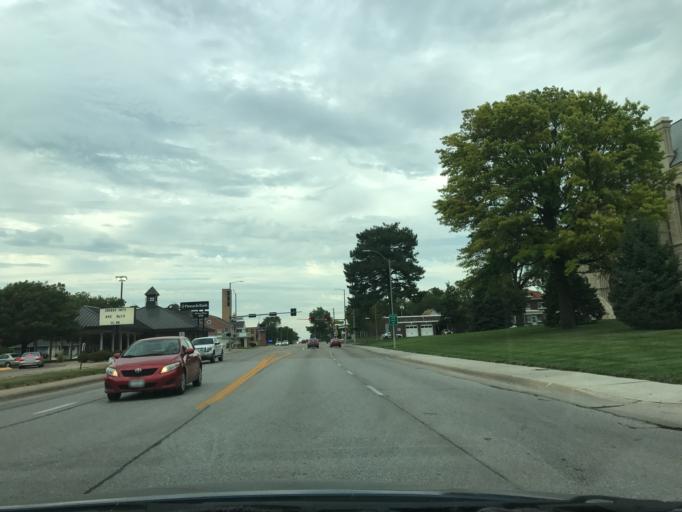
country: US
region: Nebraska
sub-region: Gage County
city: Beatrice
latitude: 40.2705
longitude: -96.7466
